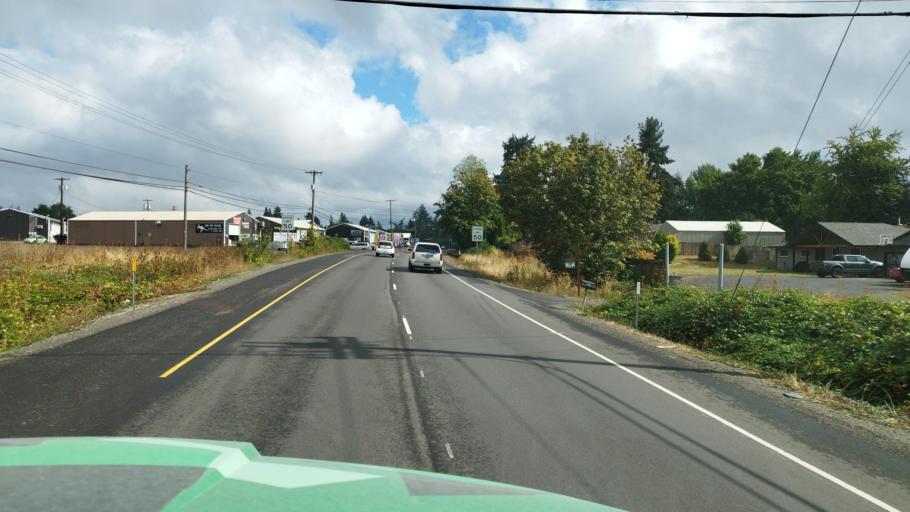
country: US
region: Oregon
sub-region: Yamhill County
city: Lafayette
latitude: 45.2332
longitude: -123.1565
